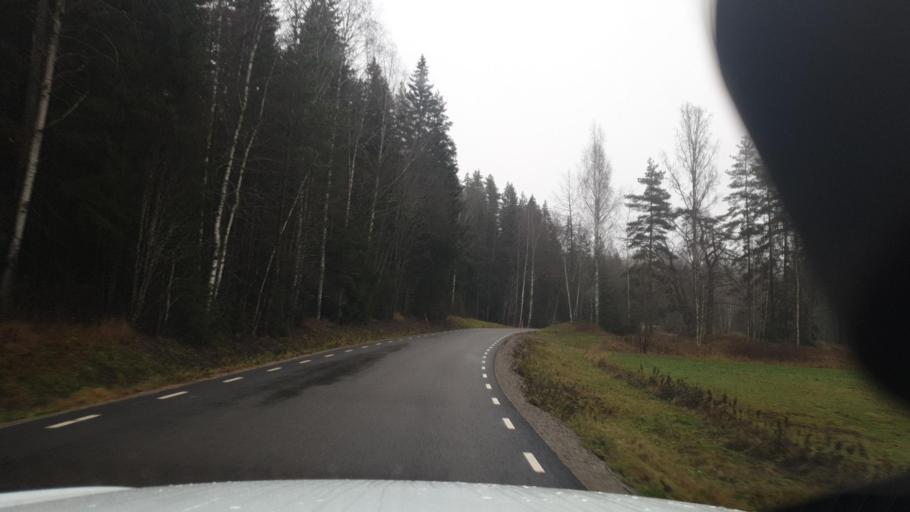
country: SE
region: Vaermland
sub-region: Arvika Kommun
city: Arvika
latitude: 59.6403
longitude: 12.8143
